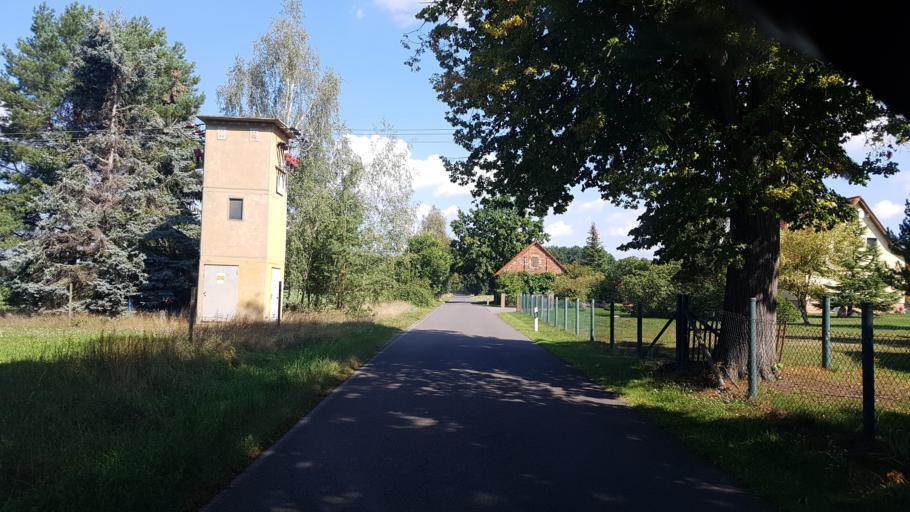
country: DE
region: Brandenburg
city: Drebkau
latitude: 51.6621
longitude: 14.2220
